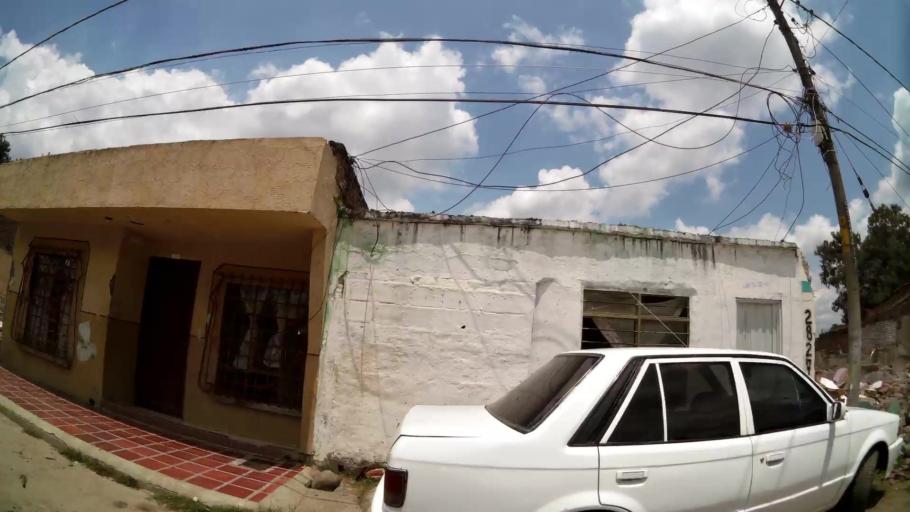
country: CO
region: Valle del Cauca
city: Cali
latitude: 3.4519
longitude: -76.4769
